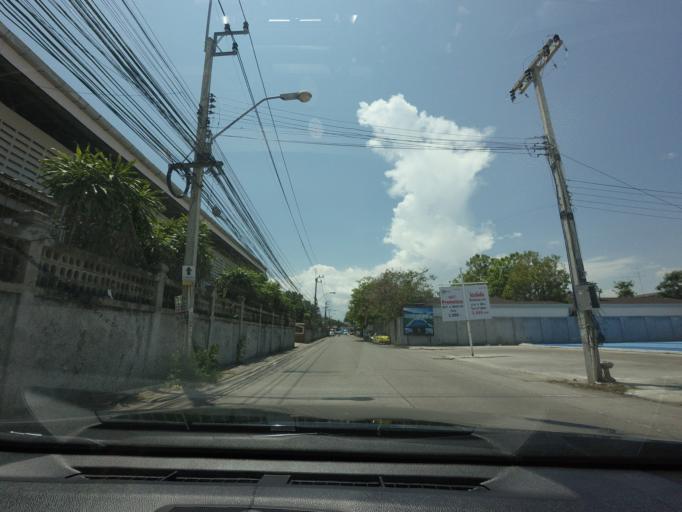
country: TH
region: Prachuap Khiri Khan
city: Hua Hin
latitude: 12.5616
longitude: 99.9576
